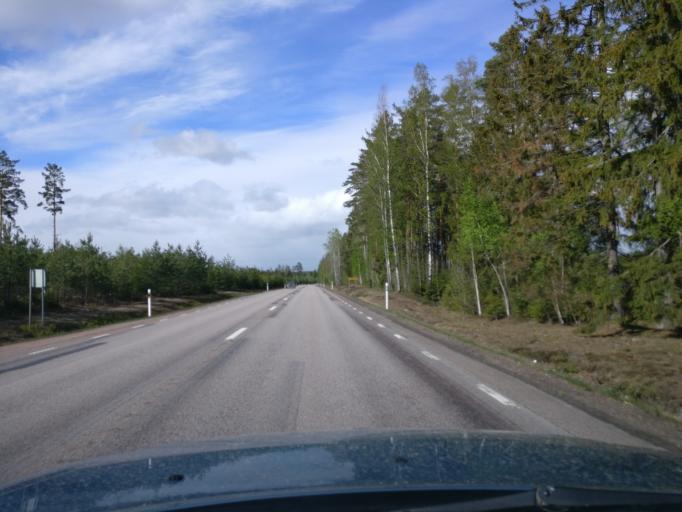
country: SE
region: Vaermland
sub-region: Forshaga Kommun
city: Forshaga
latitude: 59.5032
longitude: 13.4348
